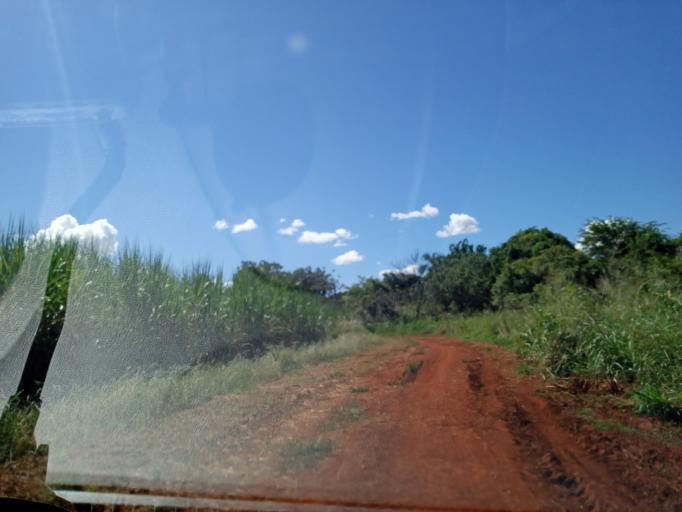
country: BR
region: Goias
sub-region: Itumbiara
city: Itumbiara
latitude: -18.4368
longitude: -49.1171
